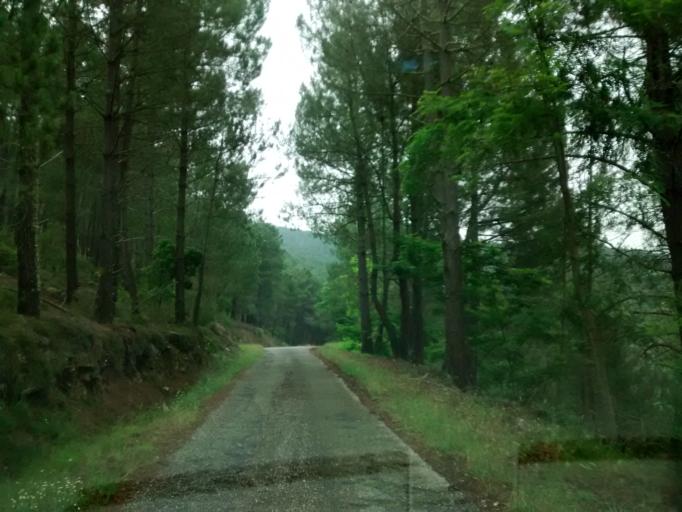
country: ES
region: Galicia
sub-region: Provincia de Ourense
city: Castro Caldelas
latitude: 42.4177
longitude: -7.3885
